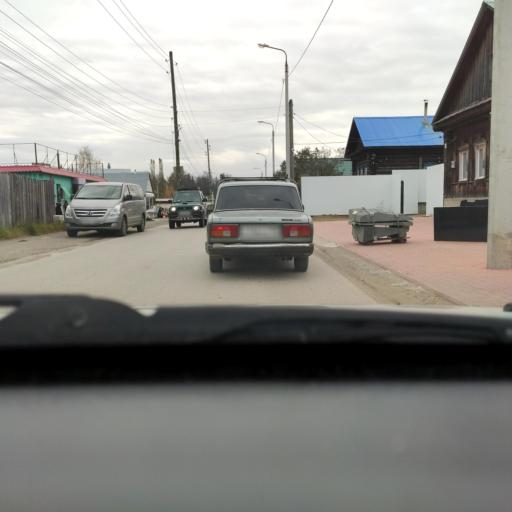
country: RU
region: Perm
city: Kondratovo
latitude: 58.0566
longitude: 56.1232
